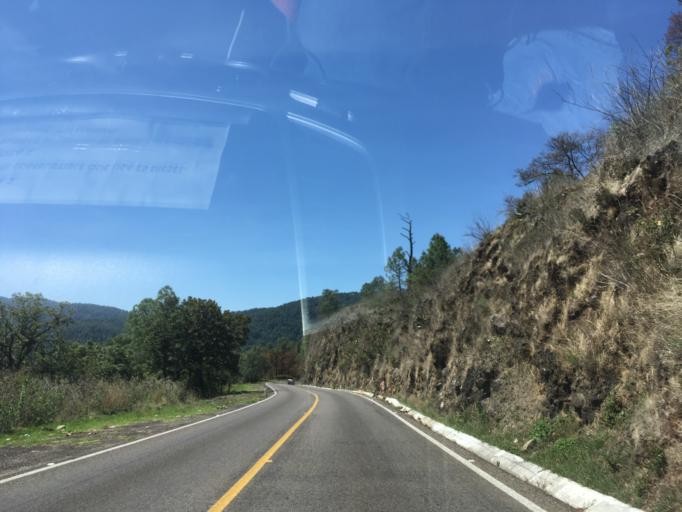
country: MX
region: Michoacan
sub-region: Hidalgo
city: Tierras Coloradas (San Pedro)
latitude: 19.6684
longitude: -100.7211
